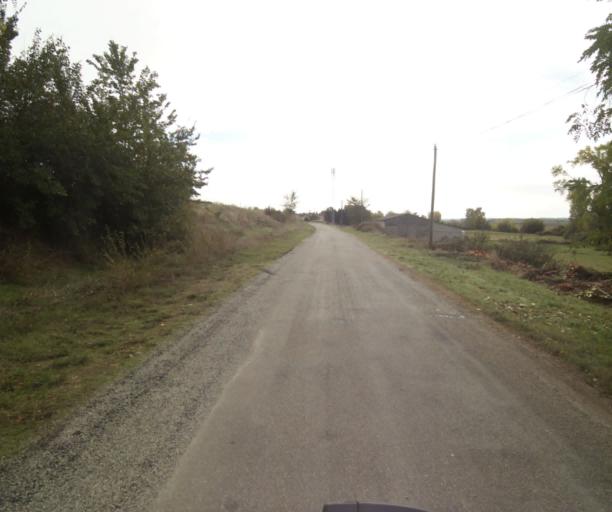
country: FR
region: Midi-Pyrenees
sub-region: Departement du Tarn-et-Garonne
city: Finhan
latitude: 43.9004
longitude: 1.2271
